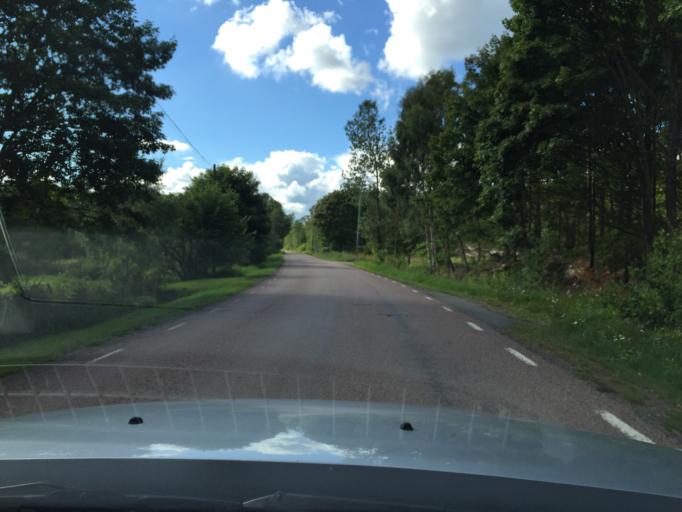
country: SE
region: Skane
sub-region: Hassleholms Kommun
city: Tormestorp
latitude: 56.0020
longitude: 13.8023
